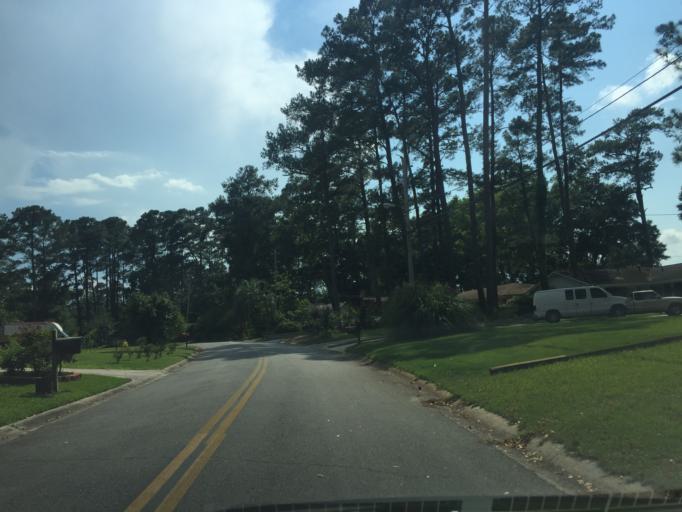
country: US
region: Georgia
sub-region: Chatham County
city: Montgomery
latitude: 31.9833
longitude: -81.1074
